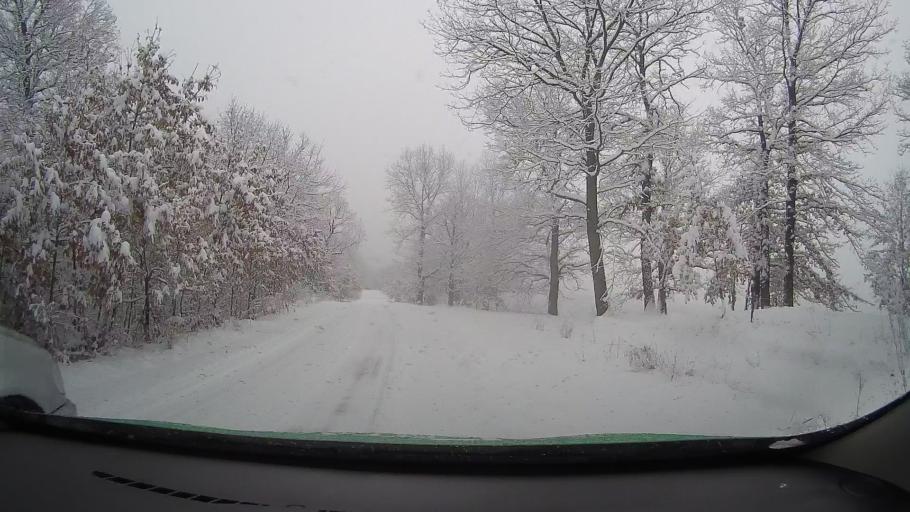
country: RO
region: Hunedoara
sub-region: Comuna Teliucu Inferior
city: Teliucu Inferior
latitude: 45.6913
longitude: 22.8931
